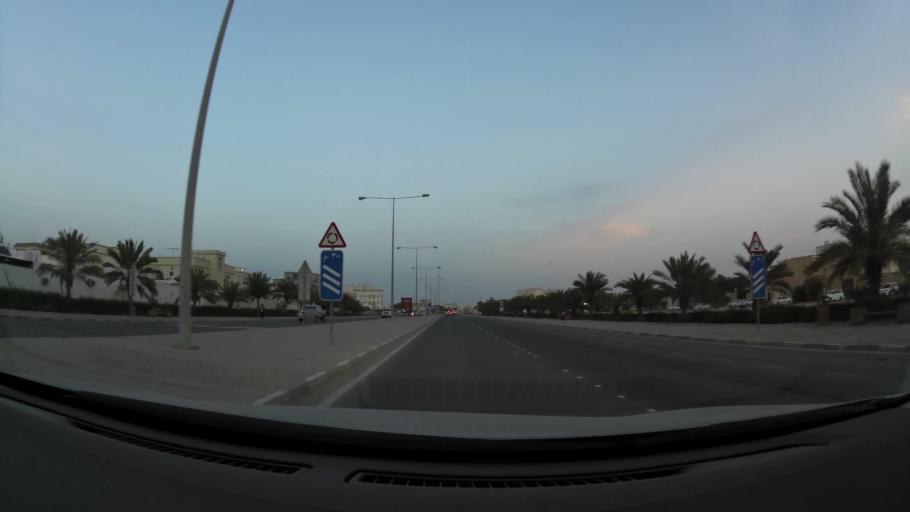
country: QA
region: Al Wakrah
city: Al Wakrah
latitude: 25.1511
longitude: 51.5997
